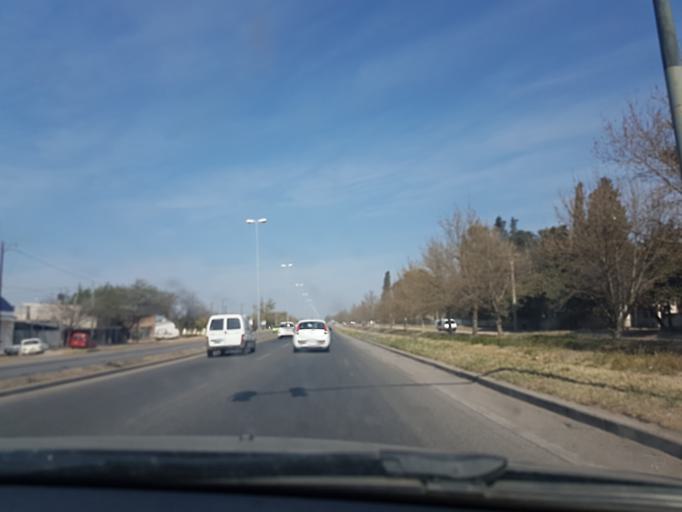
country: AR
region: Cordoba
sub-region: Departamento de Capital
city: Cordoba
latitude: -31.4759
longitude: -64.2351
